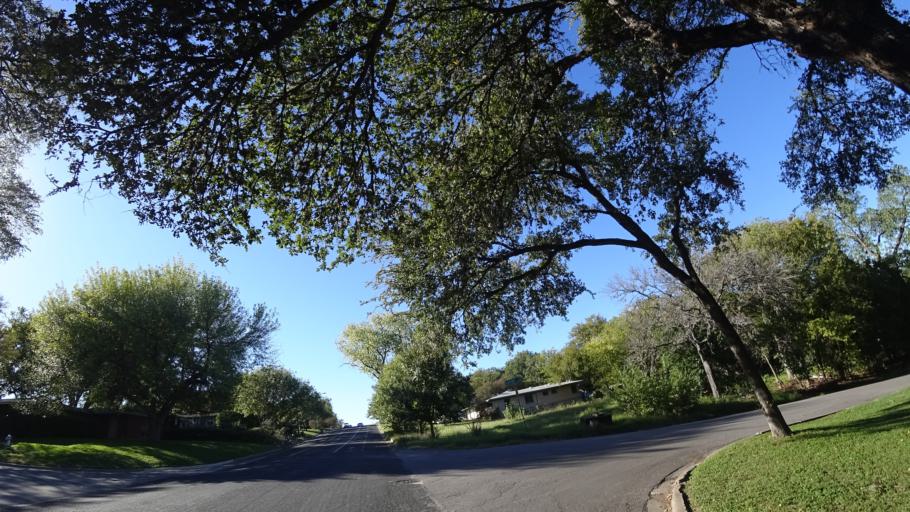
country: US
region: Texas
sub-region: Travis County
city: Austin
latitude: 30.2384
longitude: -97.7334
